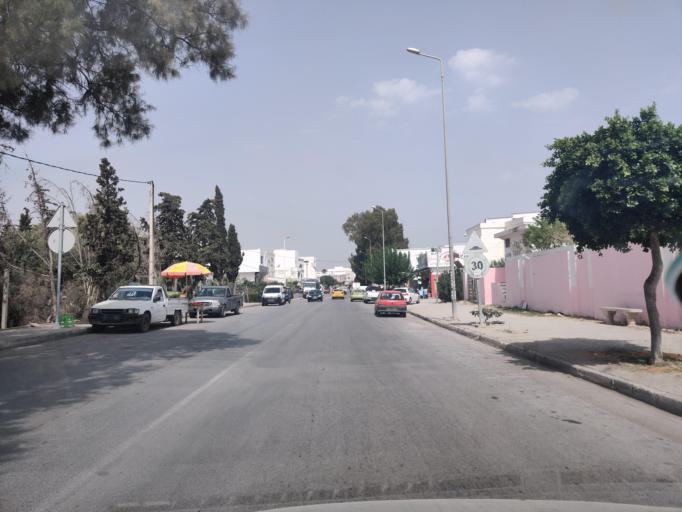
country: TN
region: Nabul
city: Al Hammamat
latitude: 36.4101
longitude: 10.6018
